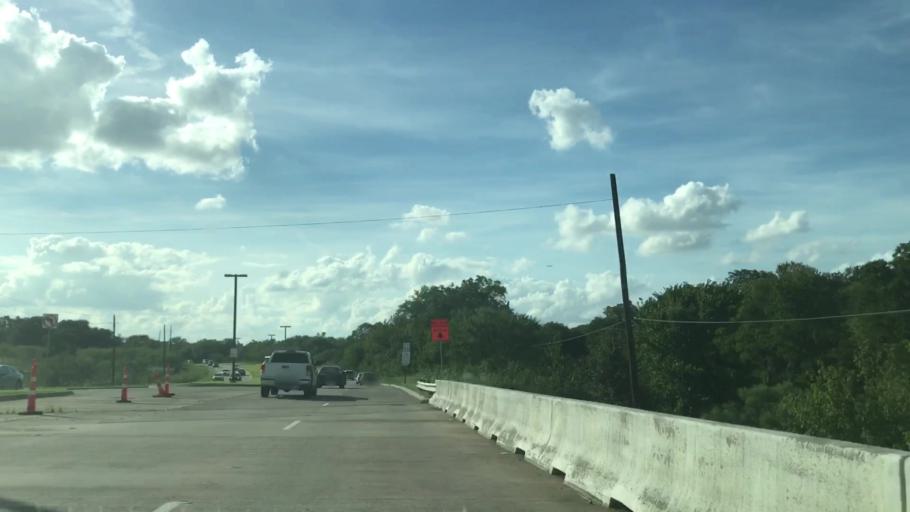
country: US
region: Texas
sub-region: Dallas County
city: Coppell
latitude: 32.9548
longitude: -96.9692
